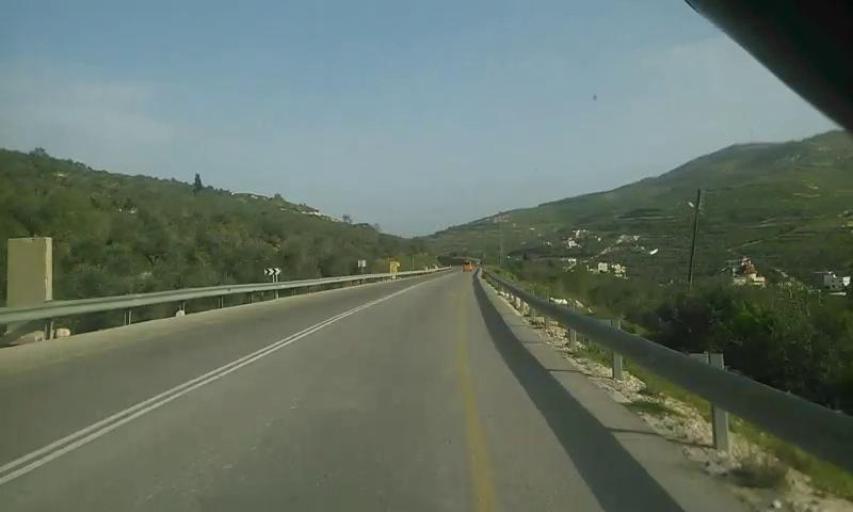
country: PS
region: West Bank
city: Madama
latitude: 32.1873
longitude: 35.2322
